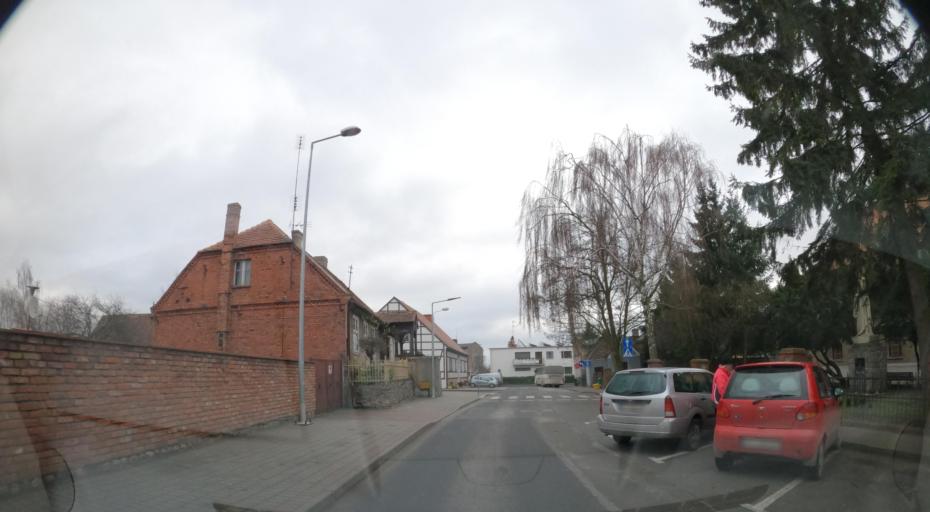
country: PL
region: Greater Poland Voivodeship
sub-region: Powiat pilski
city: Lobzenica
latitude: 53.2594
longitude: 17.2568
